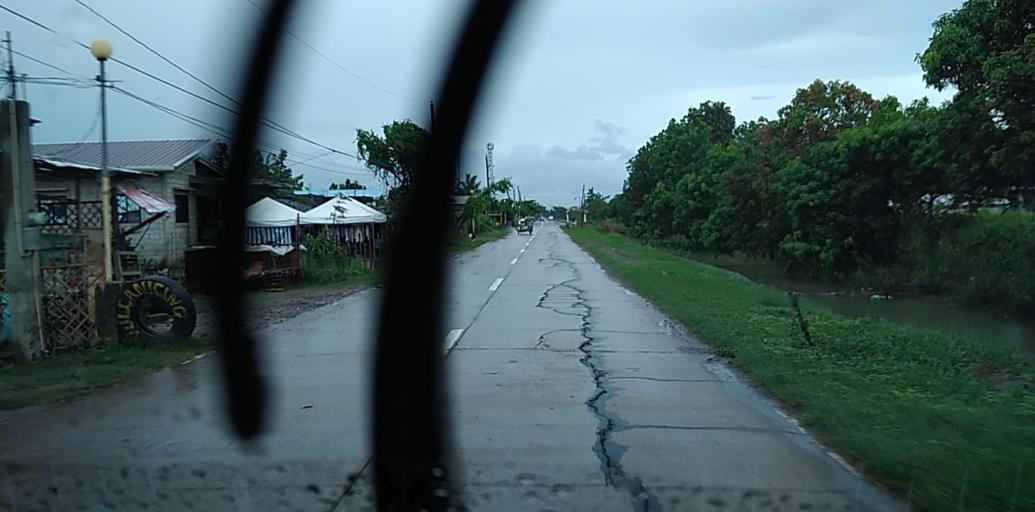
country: PH
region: Central Luzon
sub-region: Province of Pampanga
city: Salapungan
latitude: 15.1341
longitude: 120.9035
